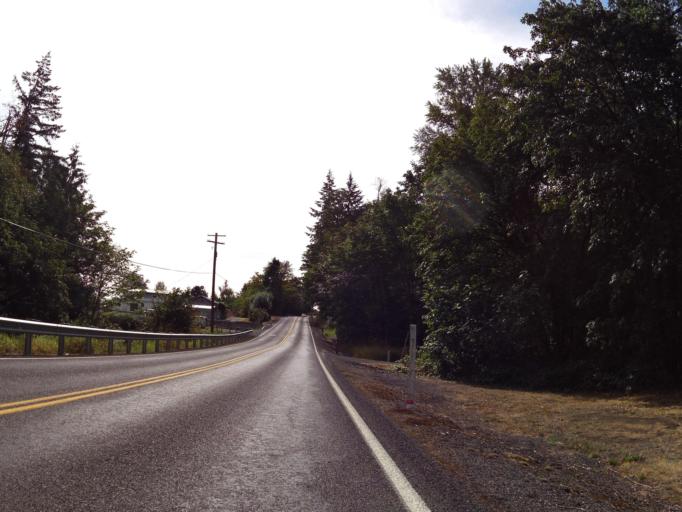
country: US
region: Washington
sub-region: Lewis County
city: Chehalis
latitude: 46.6308
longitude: -122.9689
